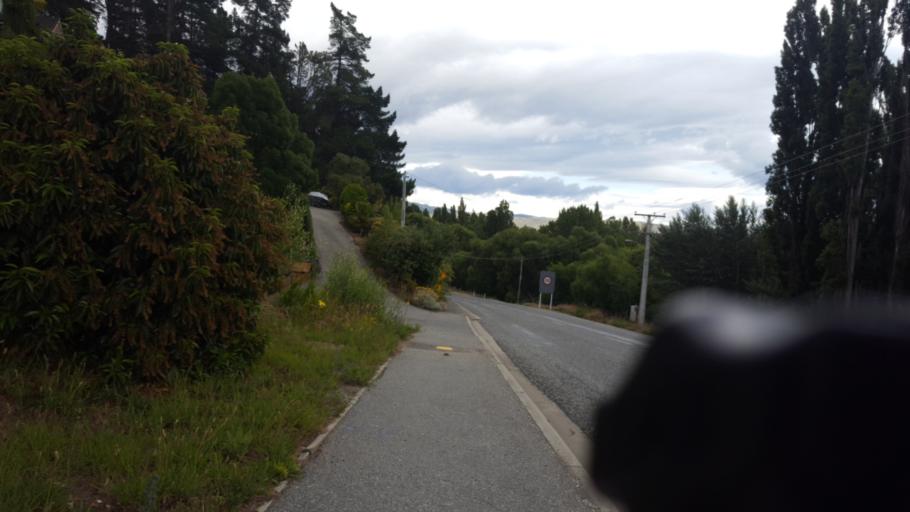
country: NZ
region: Otago
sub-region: Queenstown-Lakes District
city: Wanaka
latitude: -45.2576
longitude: 169.3817
